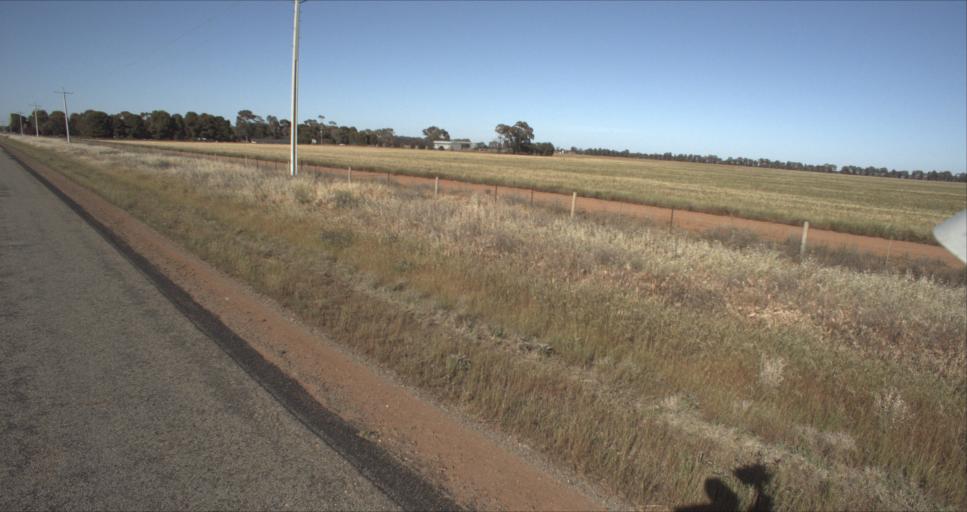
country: AU
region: New South Wales
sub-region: Leeton
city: Leeton
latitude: -34.5817
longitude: 146.2615
